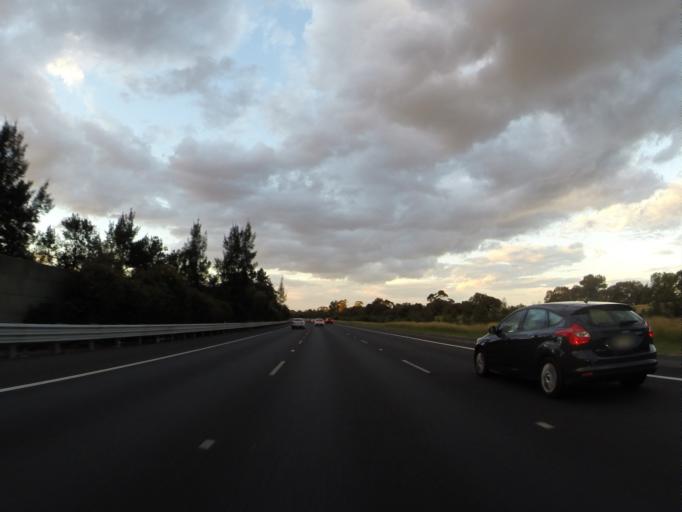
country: AU
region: New South Wales
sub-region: Campbelltown Municipality
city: Leumeah
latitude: -34.0400
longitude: 150.8223
